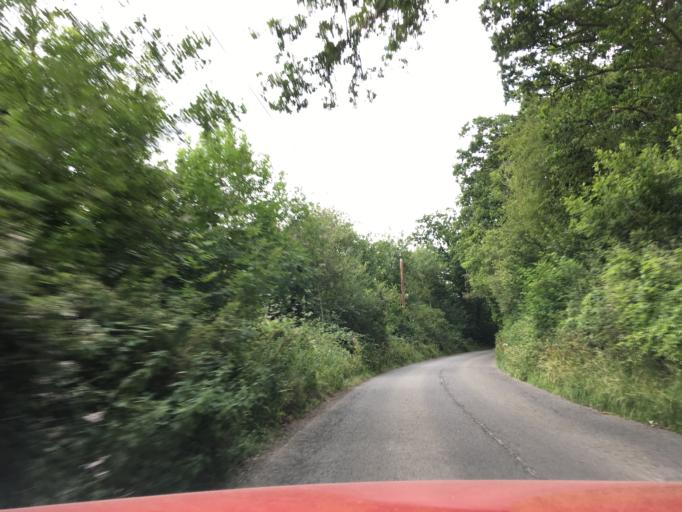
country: GB
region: England
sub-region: Oxfordshire
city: Charlbury
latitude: 51.8954
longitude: -1.5036
